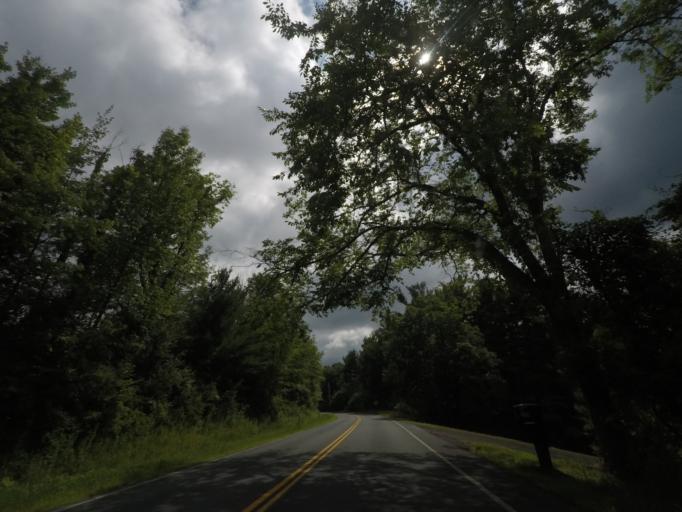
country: US
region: New York
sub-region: Saratoga County
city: Stillwater
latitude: 42.8862
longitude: -73.5613
